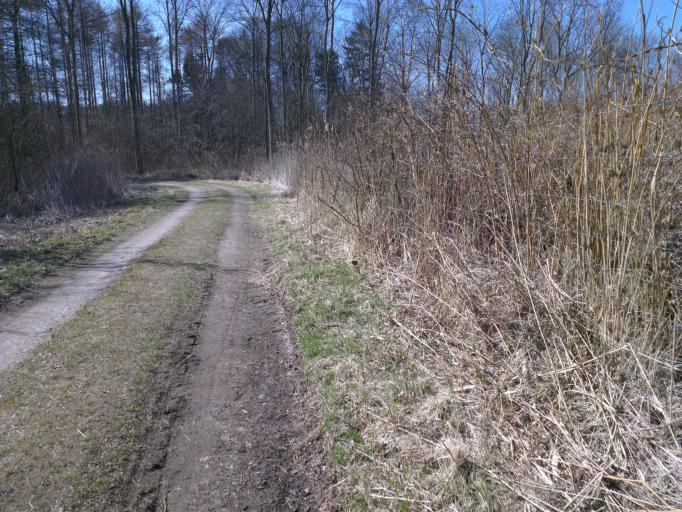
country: DK
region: Capital Region
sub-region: Frederikssund Kommune
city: Jaegerspris
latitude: 55.9271
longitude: 11.9410
